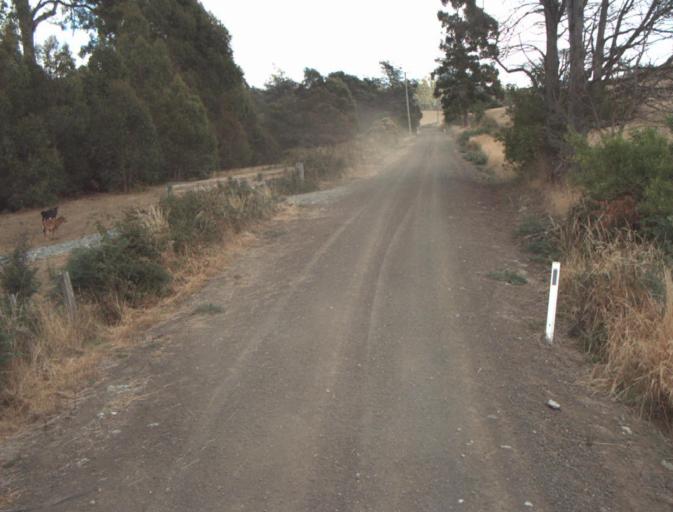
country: AU
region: Tasmania
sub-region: Launceston
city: Mayfield
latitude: -41.1989
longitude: 147.2287
